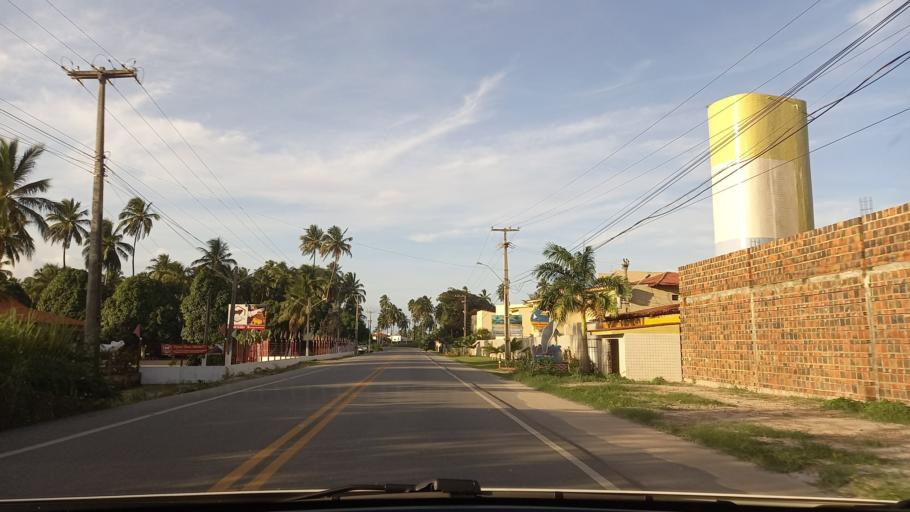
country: BR
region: Pernambuco
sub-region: Sao Jose Da Coroa Grande
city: Sao Jose da Coroa Grande
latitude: -8.9183
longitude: -35.1552
